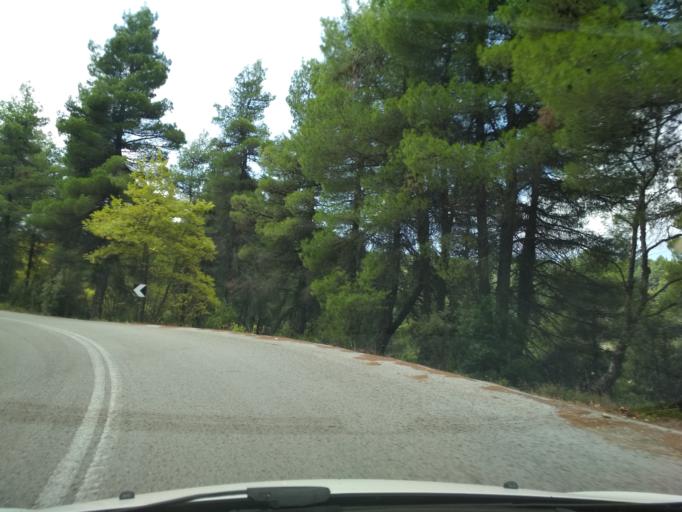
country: GR
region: Central Greece
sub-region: Nomos Evvoias
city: Politika
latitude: 38.6621
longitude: 23.5578
